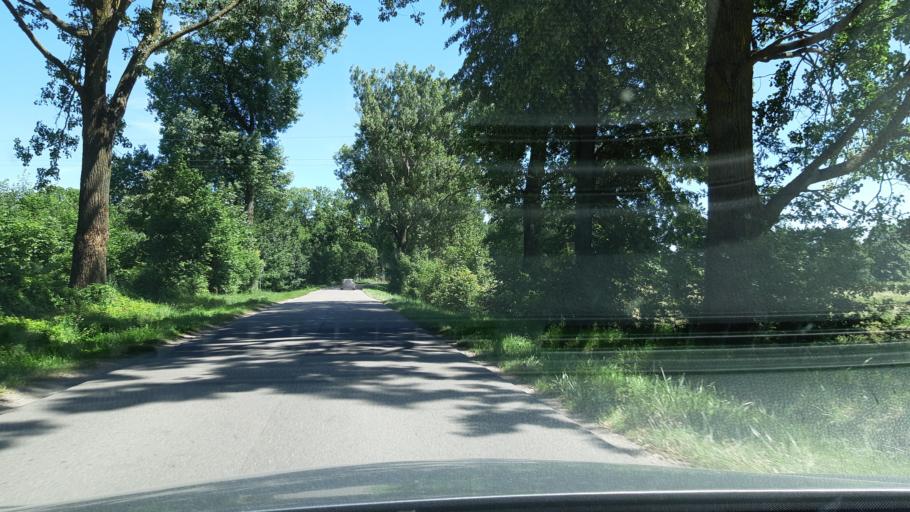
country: PL
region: Warmian-Masurian Voivodeship
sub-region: Powiat gizycki
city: Gizycko
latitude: 53.9742
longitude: 21.8071
